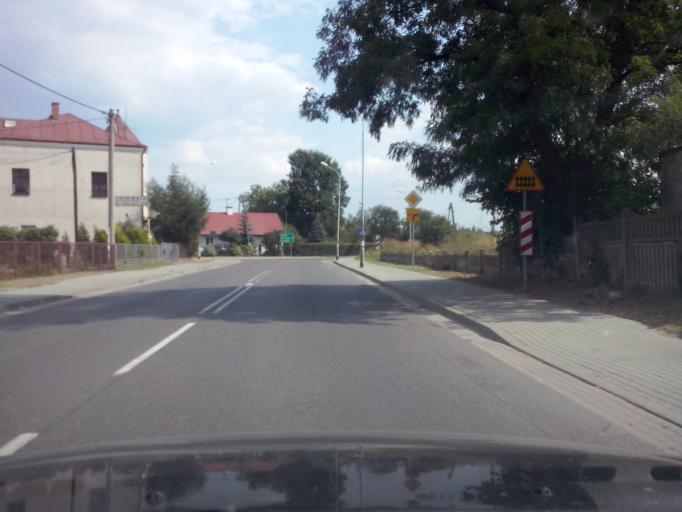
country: PL
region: Subcarpathian Voivodeship
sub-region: Powiat nizanski
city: Nisko
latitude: 50.5129
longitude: 22.1444
